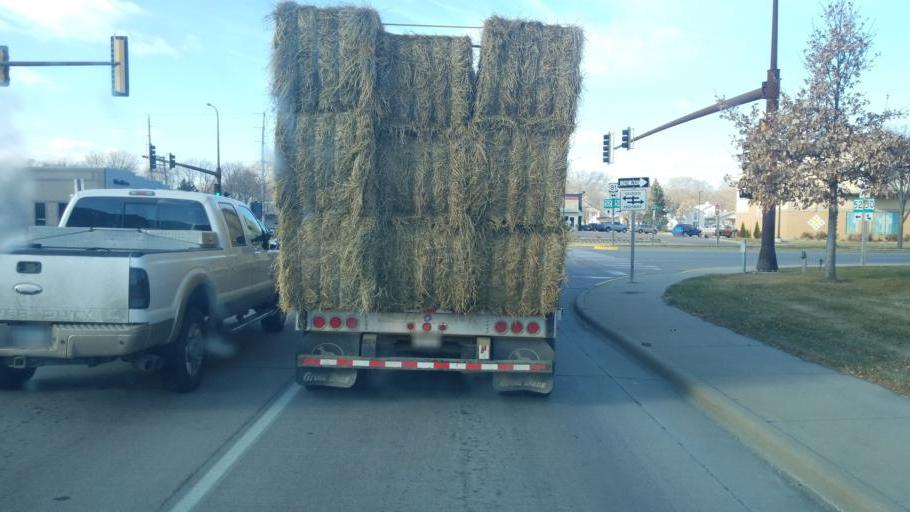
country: US
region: South Dakota
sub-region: Yankton County
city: Yankton
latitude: 42.8712
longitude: -97.3965
